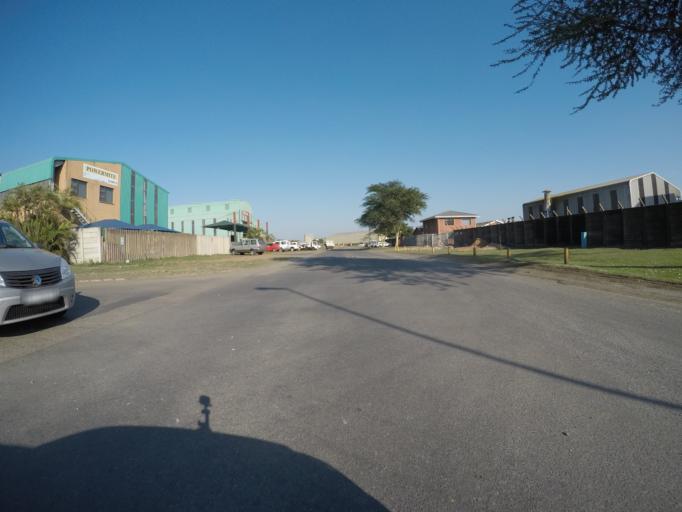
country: ZA
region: KwaZulu-Natal
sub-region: uThungulu District Municipality
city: Richards Bay
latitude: -28.7519
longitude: 32.0271
